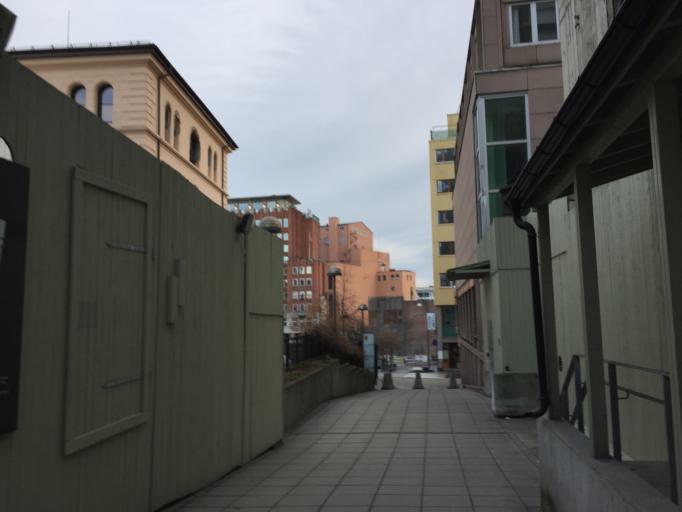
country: NO
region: Oslo
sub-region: Oslo
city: Oslo
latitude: 59.9152
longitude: 10.7470
